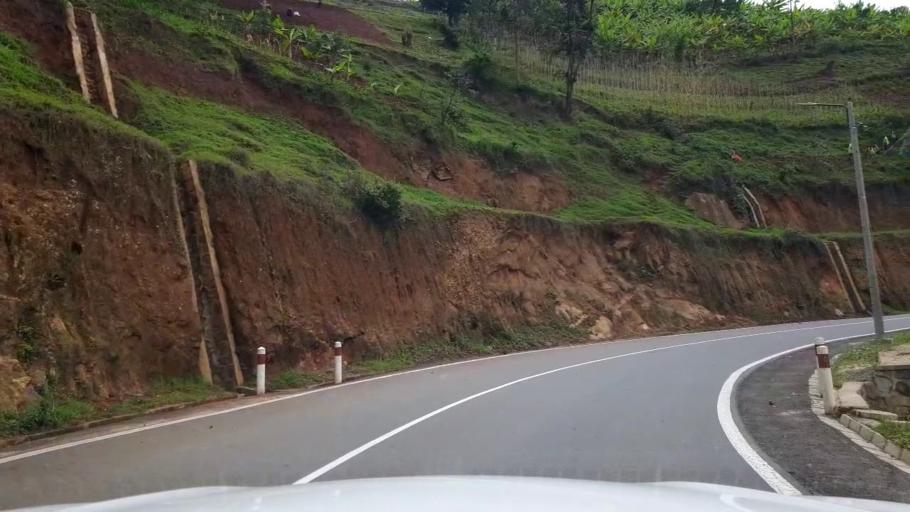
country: RW
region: Western Province
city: Kibuye
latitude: -1.9285
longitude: 29.3735
